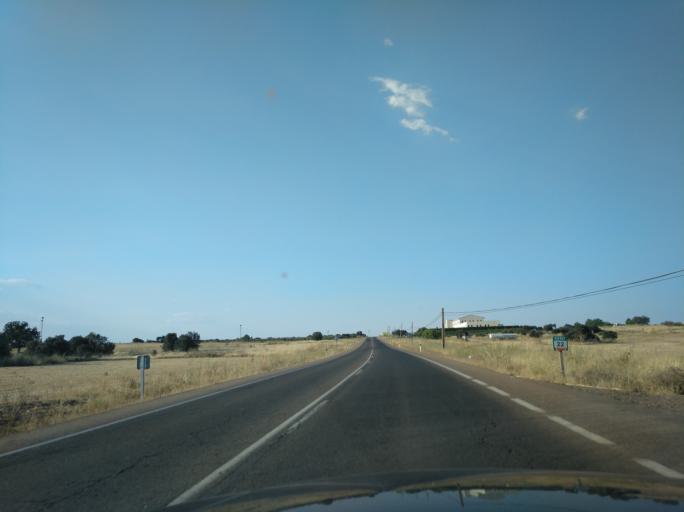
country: ES
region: Extremadura
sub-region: Provincia de Badajoz
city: Olivenza
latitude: 38.7053
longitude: -7.0869
